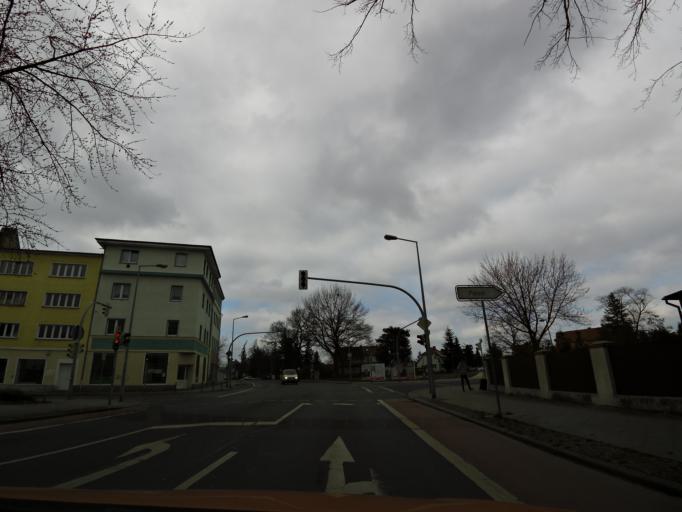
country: DE
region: Brandenburg
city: Rathenow
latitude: 52.6120
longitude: 12.3482
